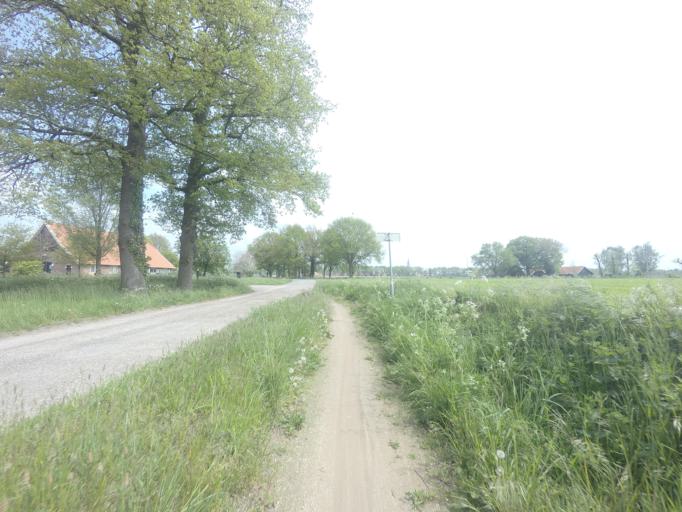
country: NL
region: Overijssel
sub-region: Gemeente Hof van Twente
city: Delden
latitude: 52.2656
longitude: 6.6958
